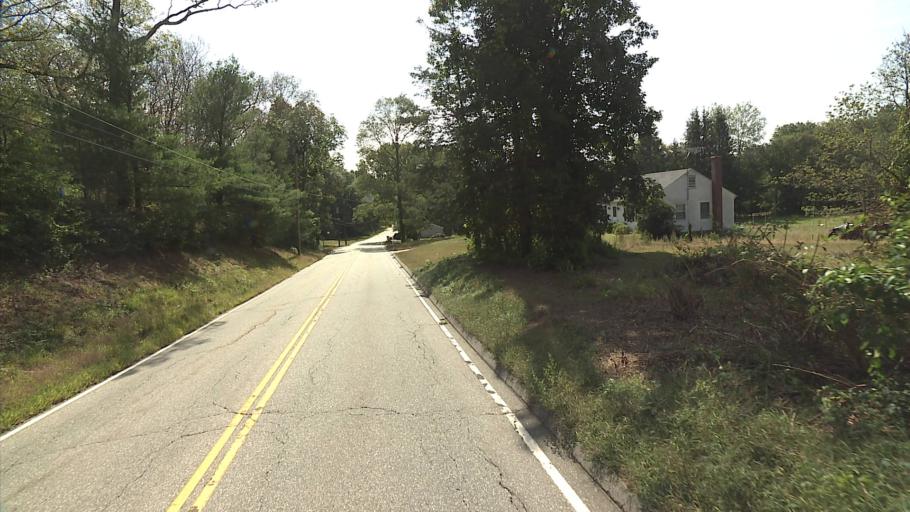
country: US
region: Connecticut
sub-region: Windham County
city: Plainfield Village
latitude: 41.6890
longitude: -71.9684
